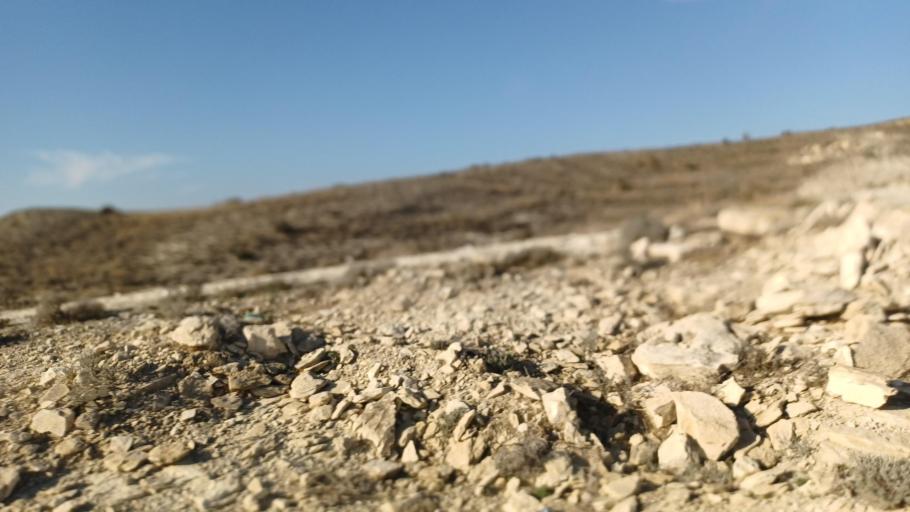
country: CY
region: Larnaka
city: Psevdas
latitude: 34.9428
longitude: 33.5195
